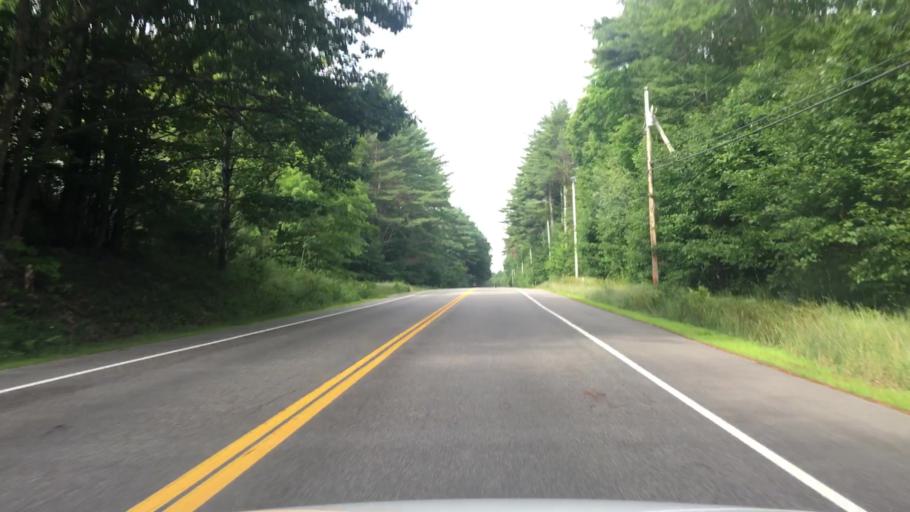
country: US
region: New Hampshire
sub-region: Carroll County
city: Sandwich
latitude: 43.8233
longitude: -71.3408
